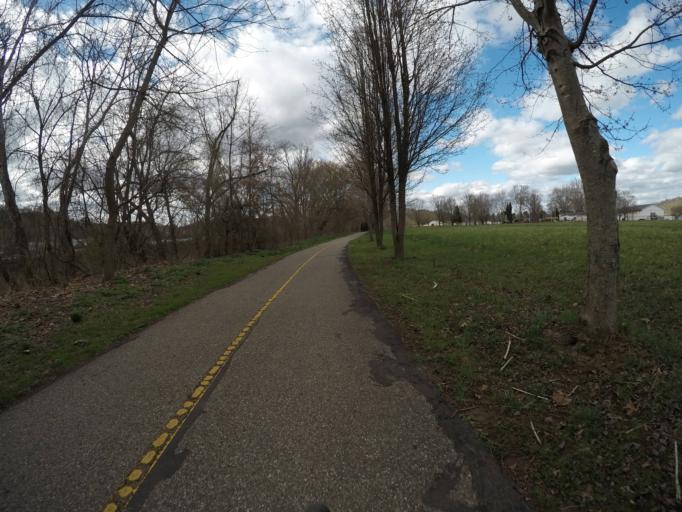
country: US
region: Ohio
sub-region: Washington County
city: Marietta
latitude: 39.4252
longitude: -81.4716
